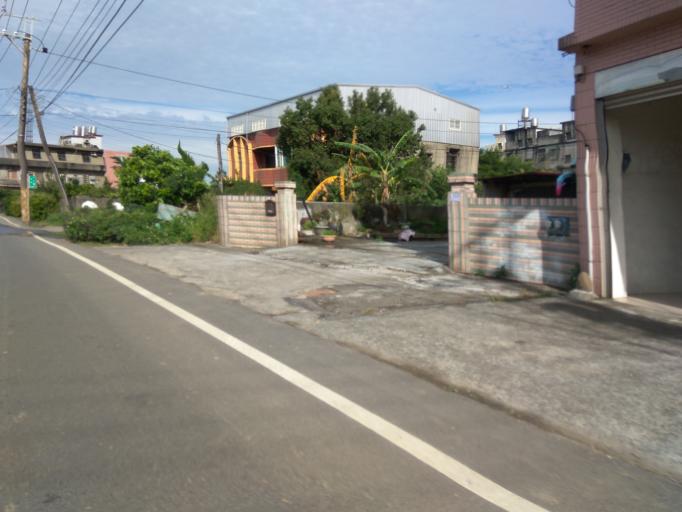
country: TW
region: Taiwan
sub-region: Hsinchu
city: Zhubei
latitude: 24.9541
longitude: 121.1266
